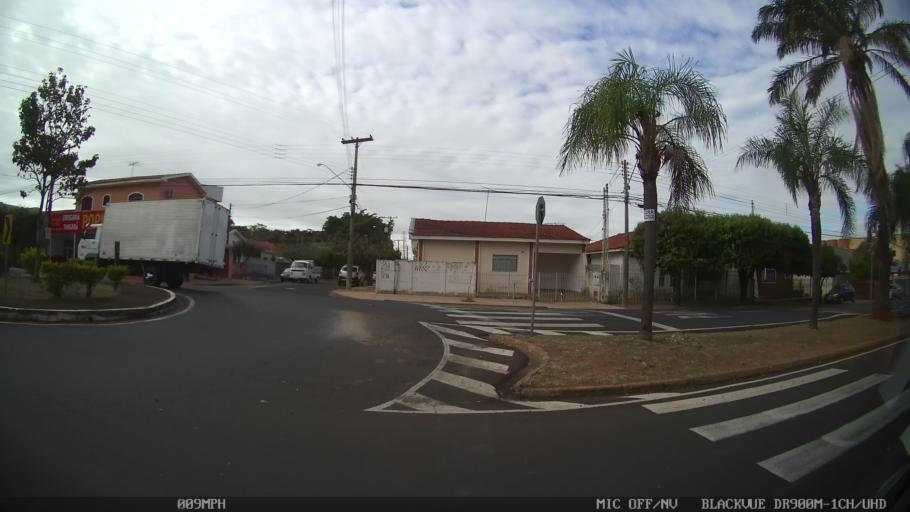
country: BR
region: Sao Paulo
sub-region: Sao Jose Do Rio Preto
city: Sao Jose do Rio Preto
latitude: -20.8411
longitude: -49.3778
